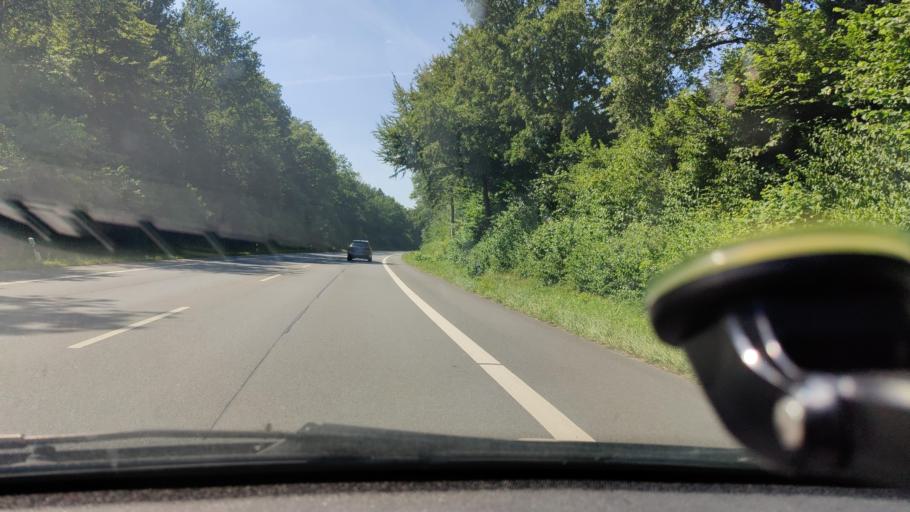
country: DE
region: North Rhine-Westphalia
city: Dorsten
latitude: 51.6527
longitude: 6.9183
